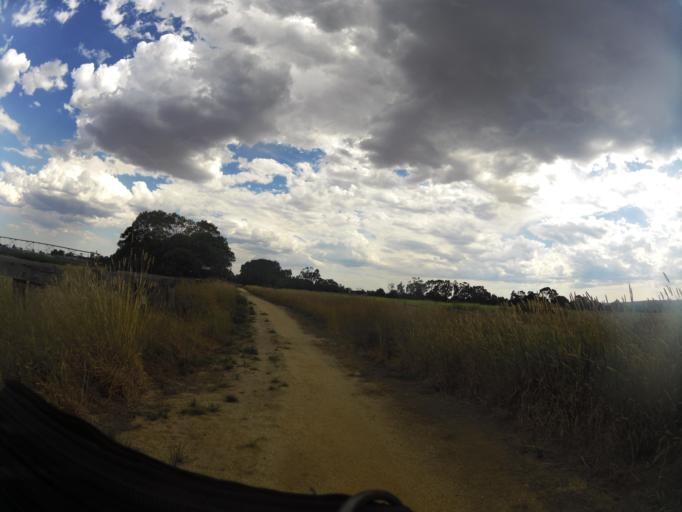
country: AU
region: Victoria
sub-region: Wellington
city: Heyfield
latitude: -38.0052
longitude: 146.6971
